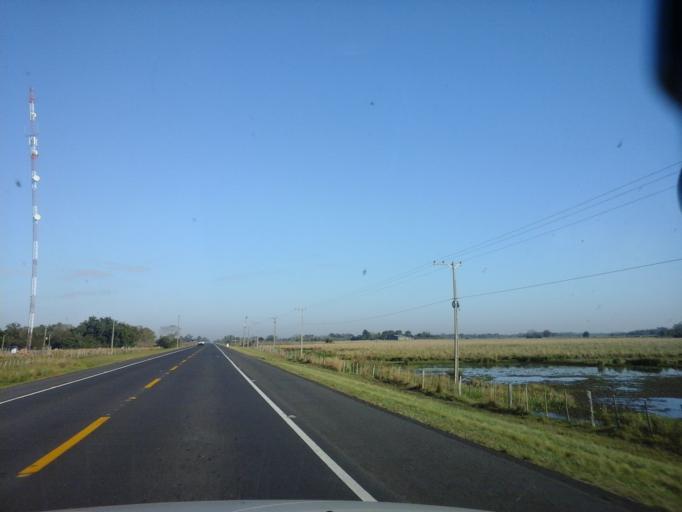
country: PY
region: Neembucu
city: Pilar
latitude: -26.8583
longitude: -58.0059
